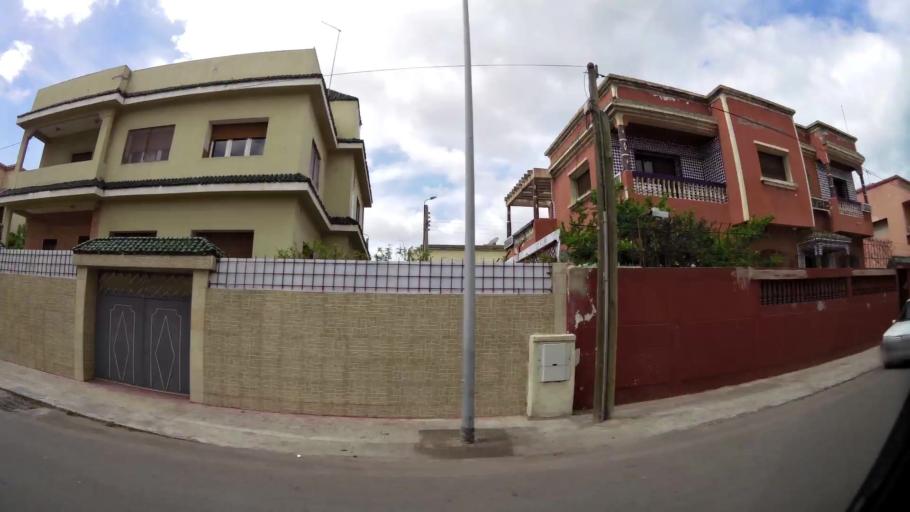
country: MA
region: Grand Casablanca
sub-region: Casablanca
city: Casablanca
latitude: 33.6133
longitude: -7.5402
